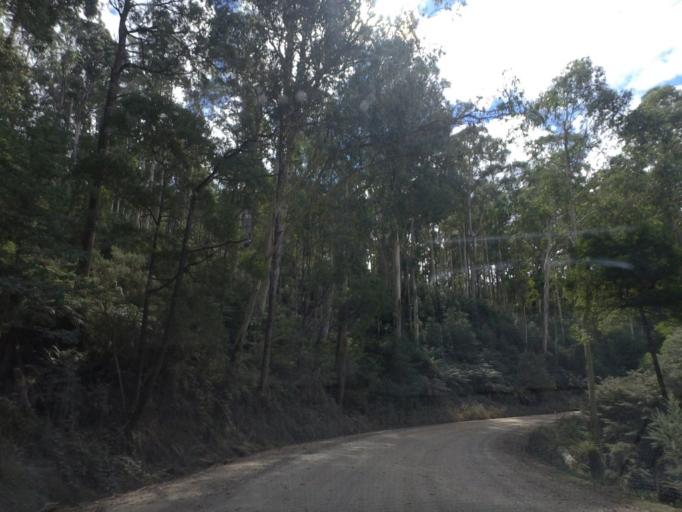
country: AU
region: Victoria
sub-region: Yarra Ranges
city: Millgrove
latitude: -37.5267
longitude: 145.9428
